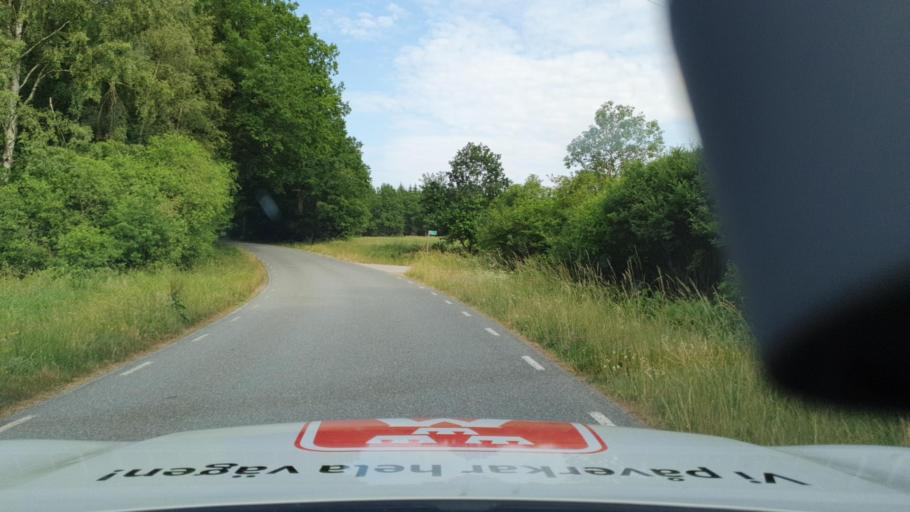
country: SE
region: Skane
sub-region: Kristianstads Kommun
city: Degeberga
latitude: 55.6933
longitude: 14.0678
